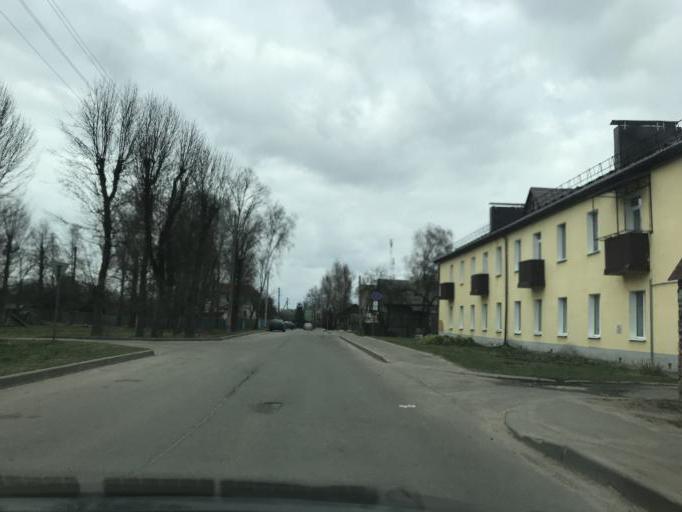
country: BY
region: Mogilev
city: Mahilyow
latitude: 53.8979
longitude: 30.3195
